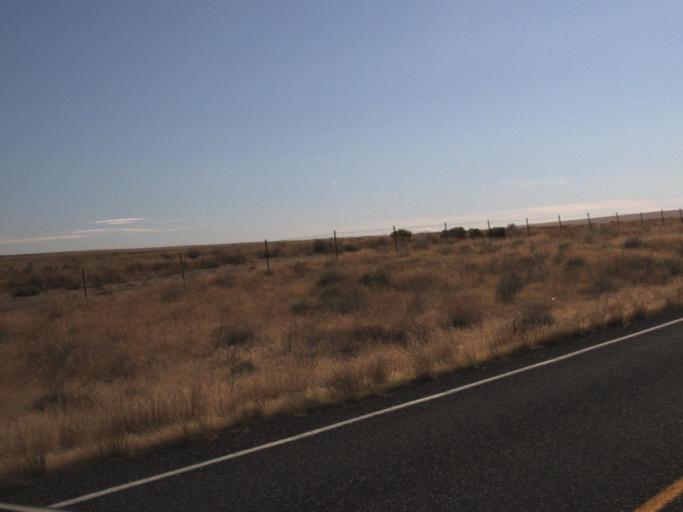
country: US
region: Washington
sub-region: Grant County
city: Desert Aire
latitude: 46.5355
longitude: -119.6840
